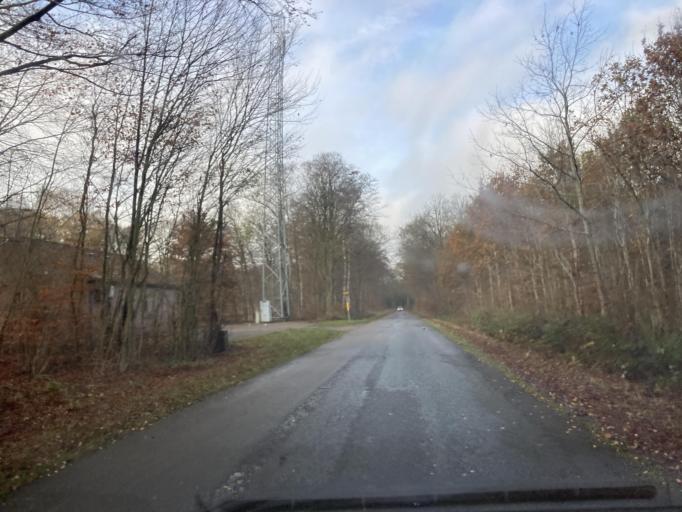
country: DK
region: Zealand
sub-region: Lolland Kommune
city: Rodby
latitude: 54.7851
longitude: 11.3732
